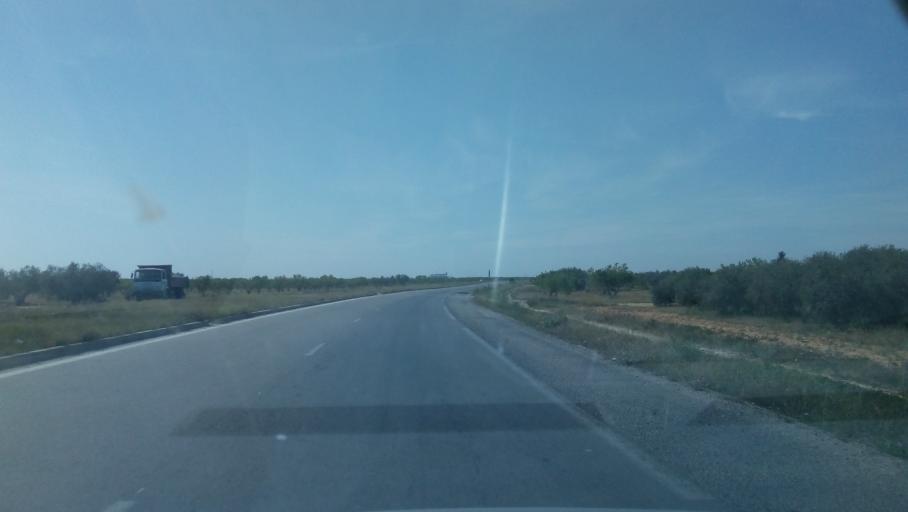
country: TN
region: Safaqis
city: Al Qarmadah
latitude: 34.8606
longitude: 10.7953
